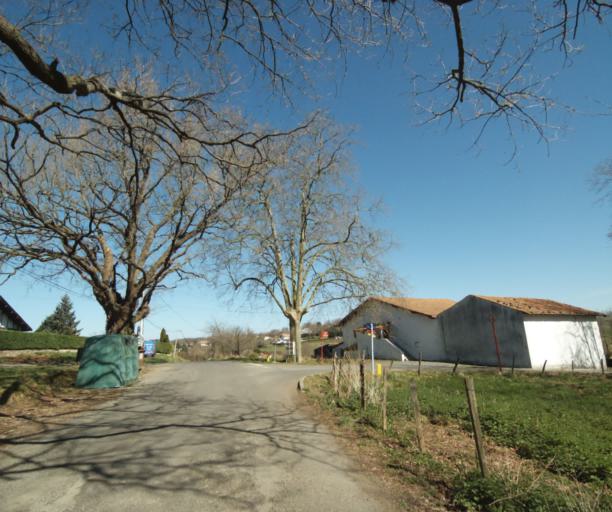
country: FR
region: Aquitaine
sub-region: Departement des Pyrenees-Atlantiques
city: Urrugne
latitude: 43.3459
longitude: -1.7175
